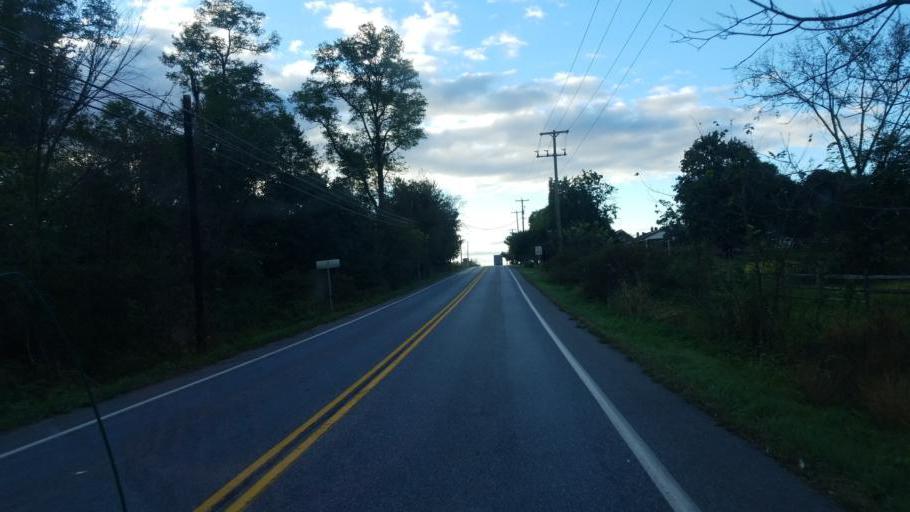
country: US
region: Pennsylvania
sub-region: Adams County
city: Lake Meade
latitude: 39.9369
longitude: -77.0618
